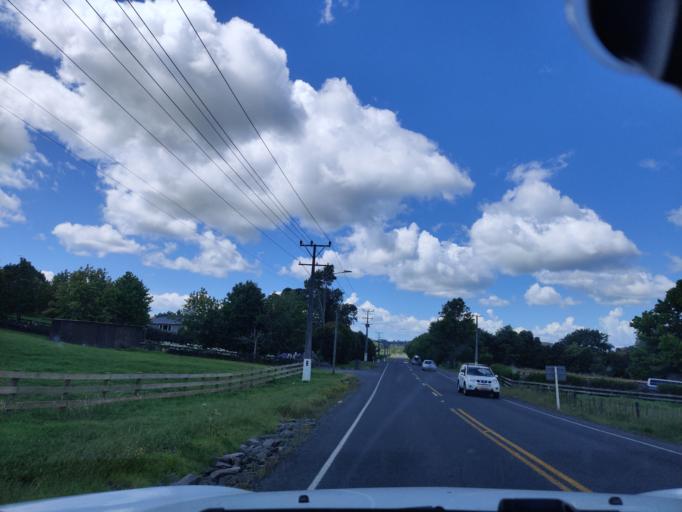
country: NZ
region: Auckland
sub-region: Auckland
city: Red Hill
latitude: -37.0120
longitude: 174.9508
